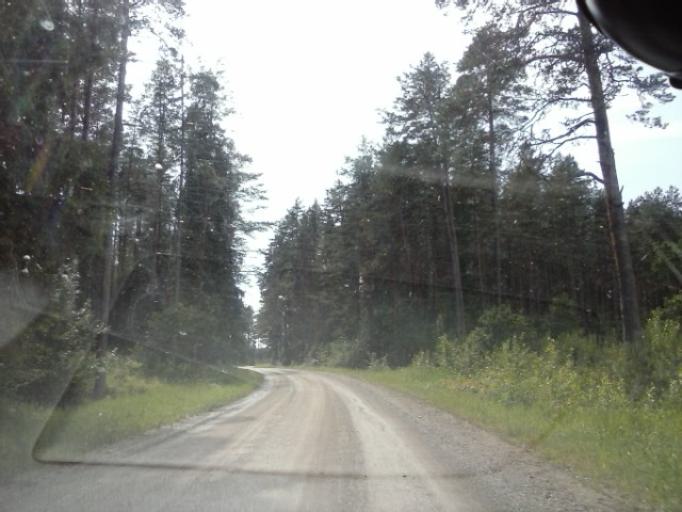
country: EE
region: Polvamaa
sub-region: Polva linn
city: Polva
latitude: 58.2550
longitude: 26.9838
